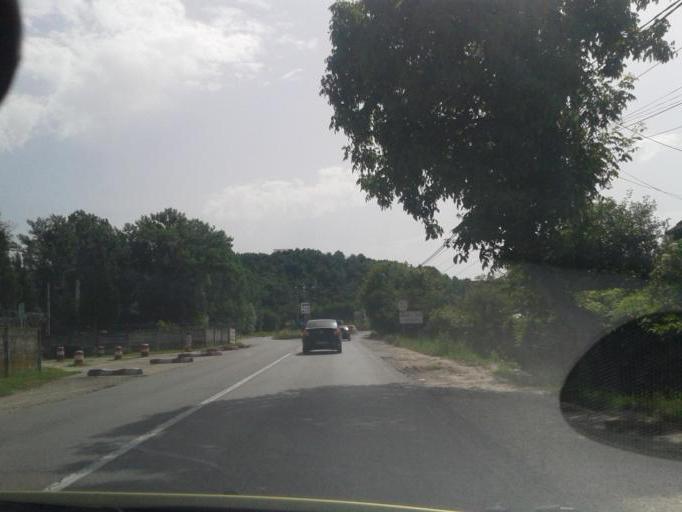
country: RO
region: Valcea
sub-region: Municipiul Ramnicu Valcea
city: Goranu
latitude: 45.0781
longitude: 24.3857
